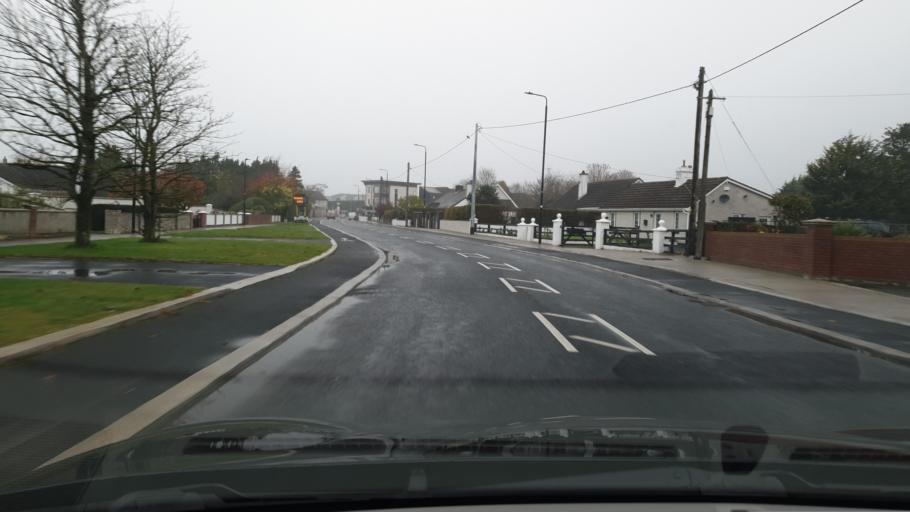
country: IE
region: Leinster
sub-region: An Mhi
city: Ashbourne
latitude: 53.5095
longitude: -6.3930
